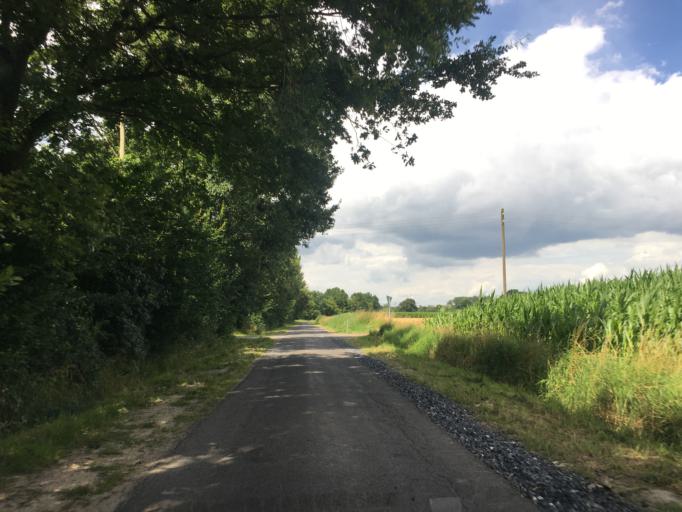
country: DE
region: North Rhine-Westphalia
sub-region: Regierungsbezirk Munster
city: Muenster
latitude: 52.0271
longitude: 7.6115
